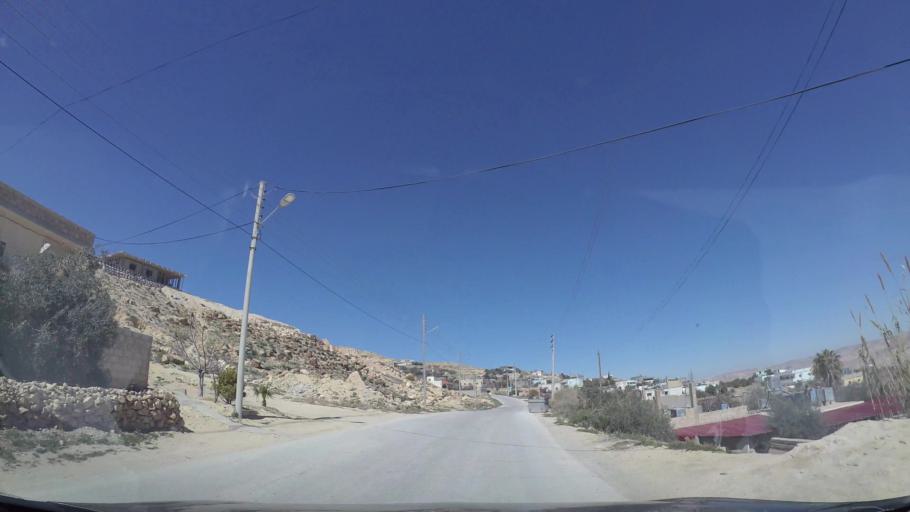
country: JO
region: Tafielah
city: At Tafilah
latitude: 30.8332
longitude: 35.5764
